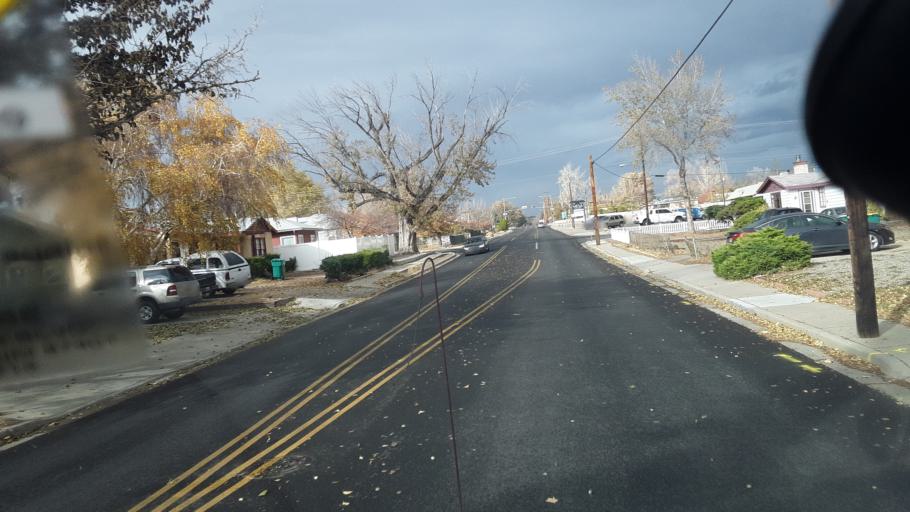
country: US
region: New Mexico
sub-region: San Juan County
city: Farmington
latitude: 36.7391
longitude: -108.1979
